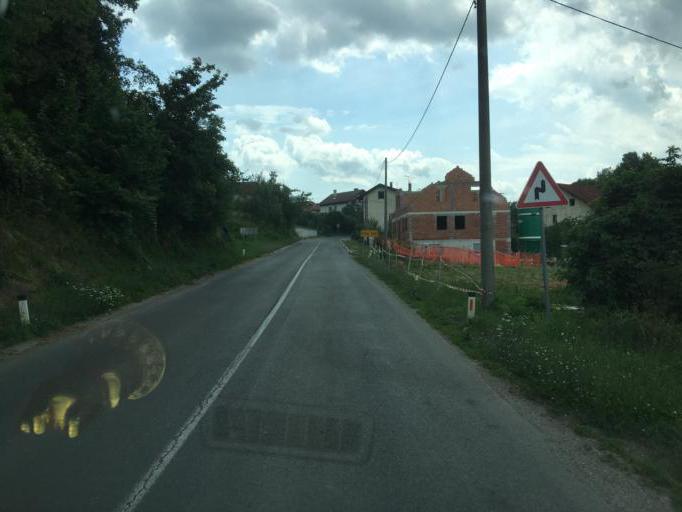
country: SI
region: Postojna
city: Postojna
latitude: 45.7854
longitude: 14.1968
